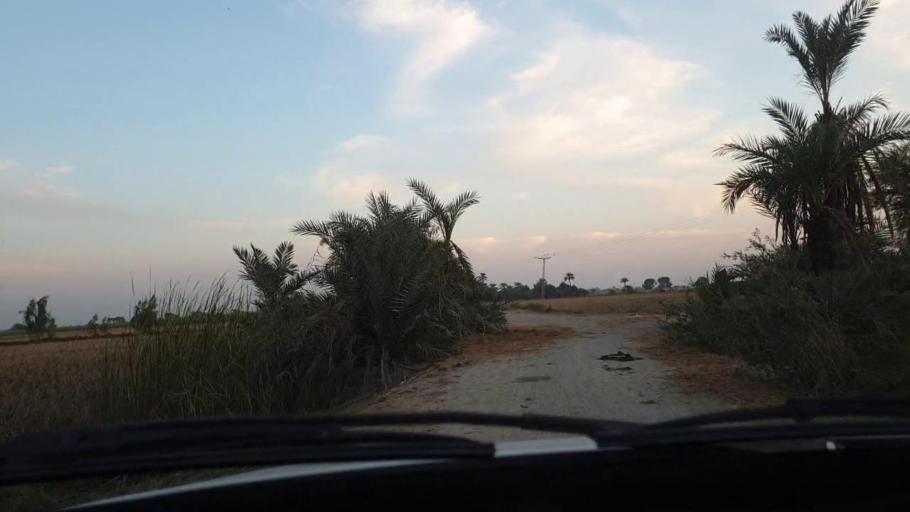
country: PK
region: Sindh
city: Tando Muhammad Khan
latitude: 25.0912
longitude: 68.3936
